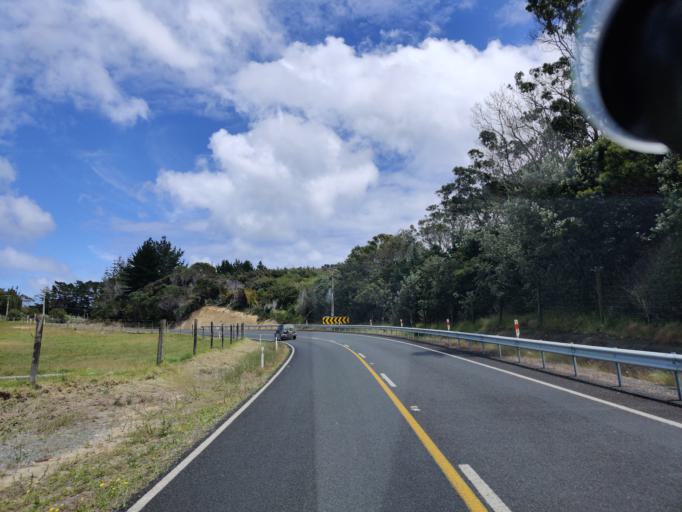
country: NZ
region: Northland
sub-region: Far North District
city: Kaitaia
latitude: -34.8878
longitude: 173.1629
